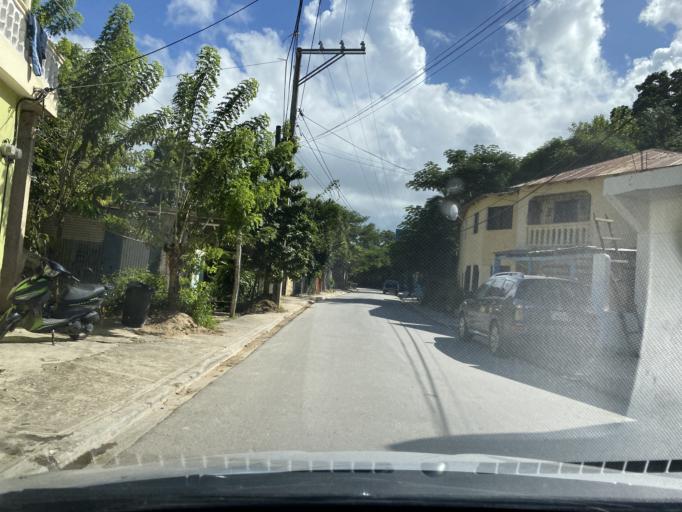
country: DO
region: Samana
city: Las Terrenas
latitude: 19.3161
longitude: -69.5299
